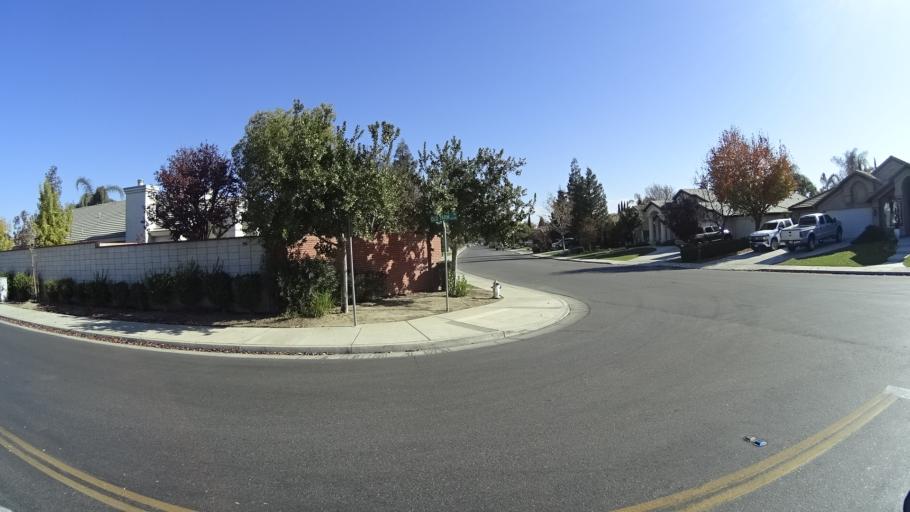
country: US
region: California
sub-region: Kern County
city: Rosedale
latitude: 35.3638
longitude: -119.1368
